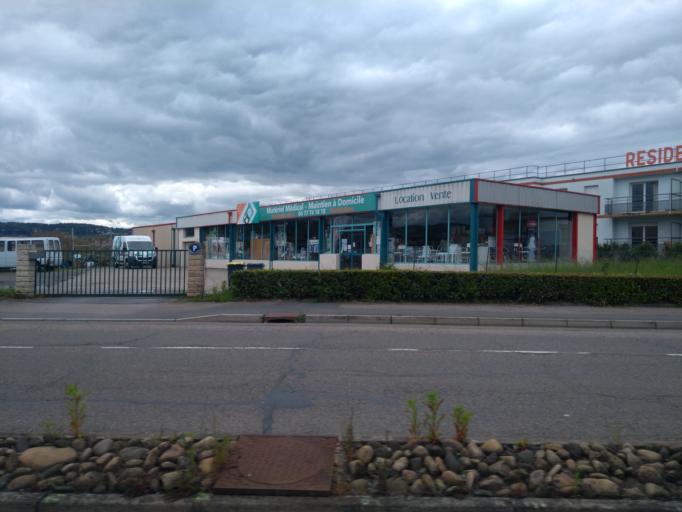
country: FR
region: Rhone-Alpes
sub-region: Departement de la Loire
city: Villars
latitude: 45.4783
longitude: 4.3641
